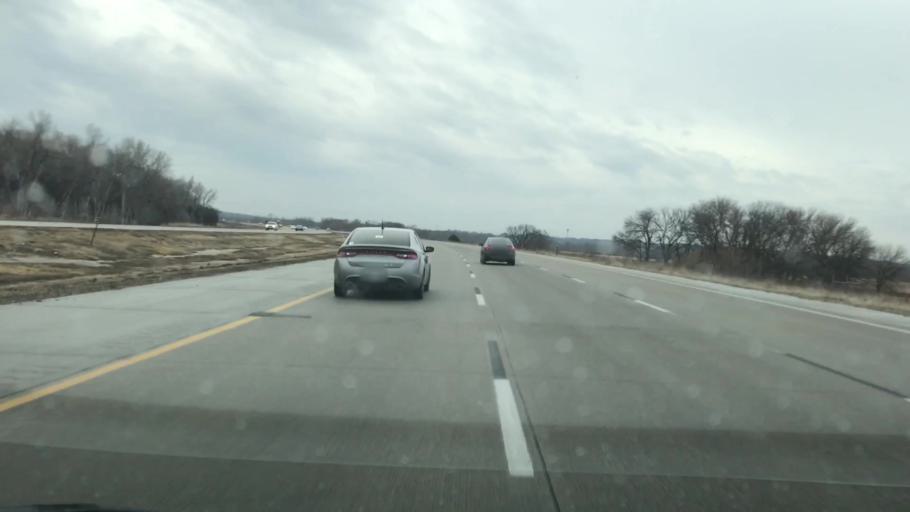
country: US
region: Nebraska
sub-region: Saunders County
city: Ashland
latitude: 41.0561
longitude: -96.2967
